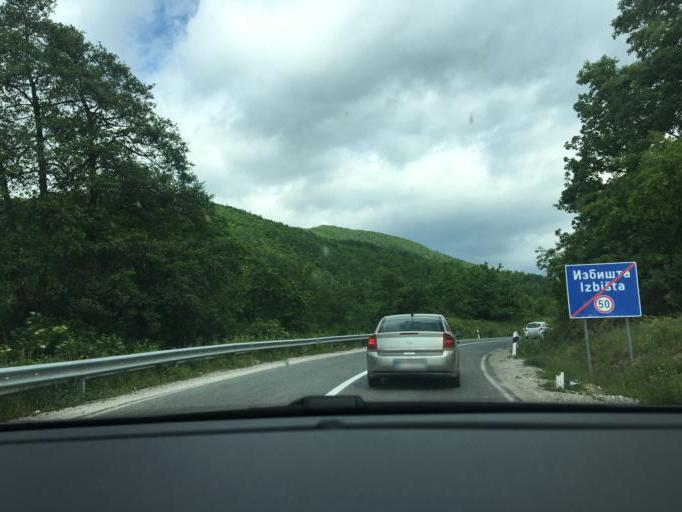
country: MK
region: Resen
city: Jankovec
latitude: 41.1345
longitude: 21.0067
